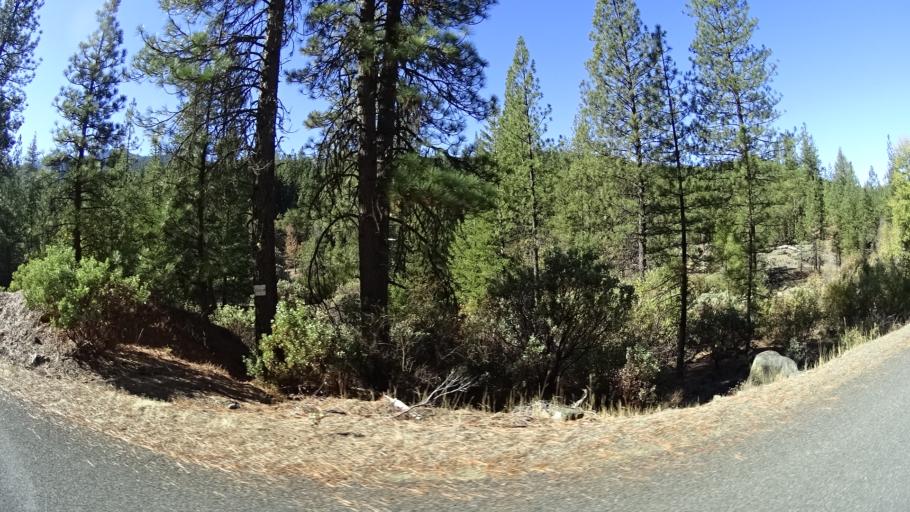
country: US
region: California
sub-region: Trinity County
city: Weaverville
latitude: 41.1166
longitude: -123.0912
